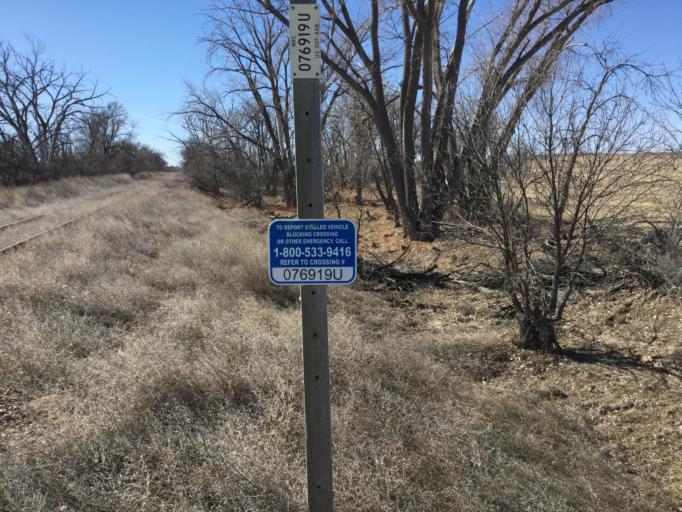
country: US
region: Kansas
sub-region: Decatur County
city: Oberlin
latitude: 39.9113
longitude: -100.7400
